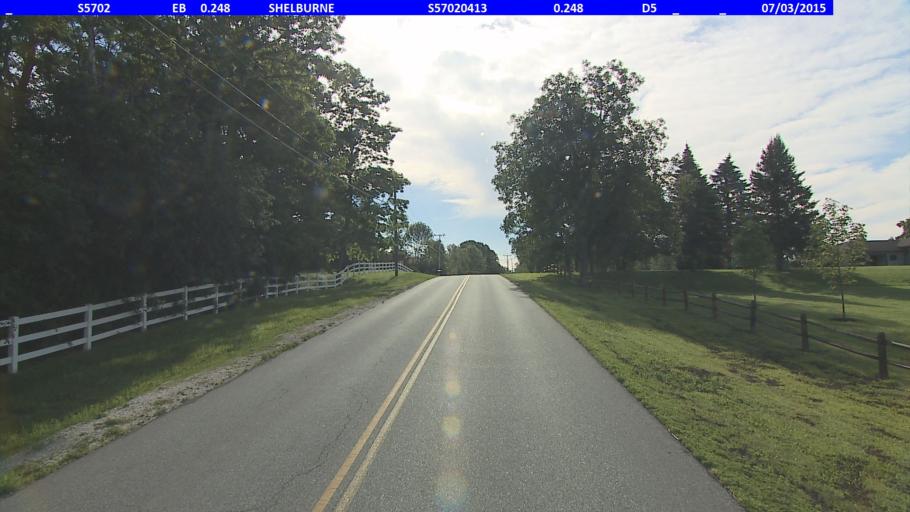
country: US
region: Vermont
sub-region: Chittenden County
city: South Burlington
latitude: 44.4088
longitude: -73.1929
